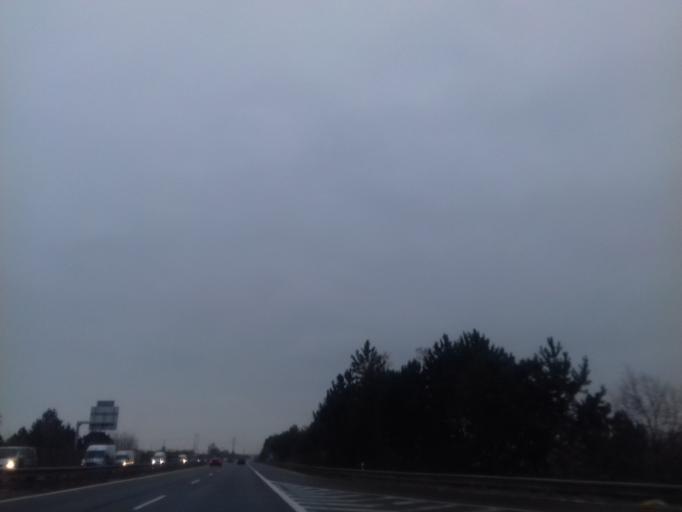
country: CZ
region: Central Bohemia
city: Zdice
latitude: 49.9009
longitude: 13.9595
